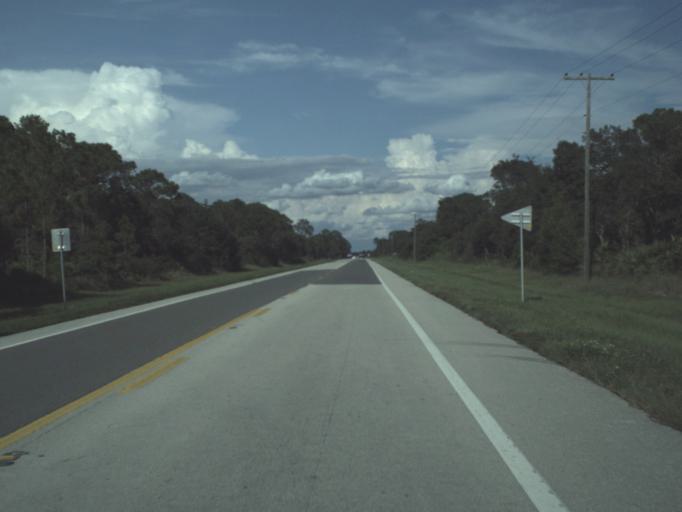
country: US
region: Florida
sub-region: Highlands County
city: Sebring
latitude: 27.4176
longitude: -81.4422
